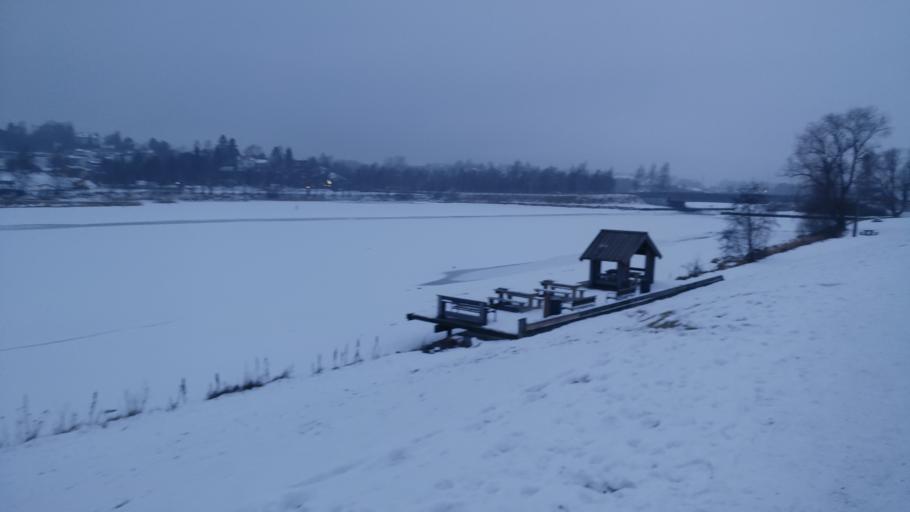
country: NO
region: Akershus
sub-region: Skedsmo
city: Lillestrom
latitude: 59.9554
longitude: 11.0320
